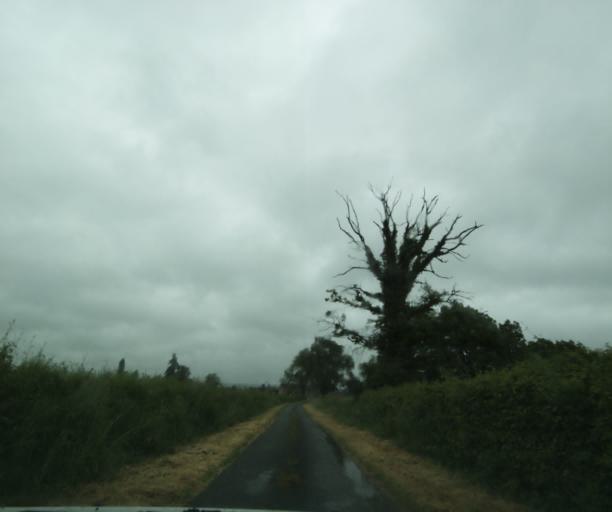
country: FR
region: Bourgogne
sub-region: Departement de Saone-et-Loire
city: Palinges
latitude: 46.5552
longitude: 4.2345
